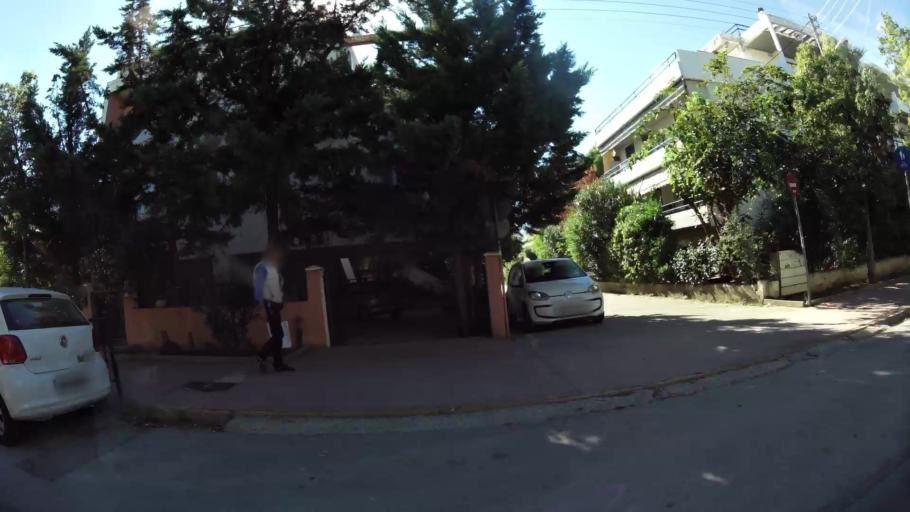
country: GR
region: Attica
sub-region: Nomarchia Athinas
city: Vrilissia
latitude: 38.0247
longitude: 23.8243
